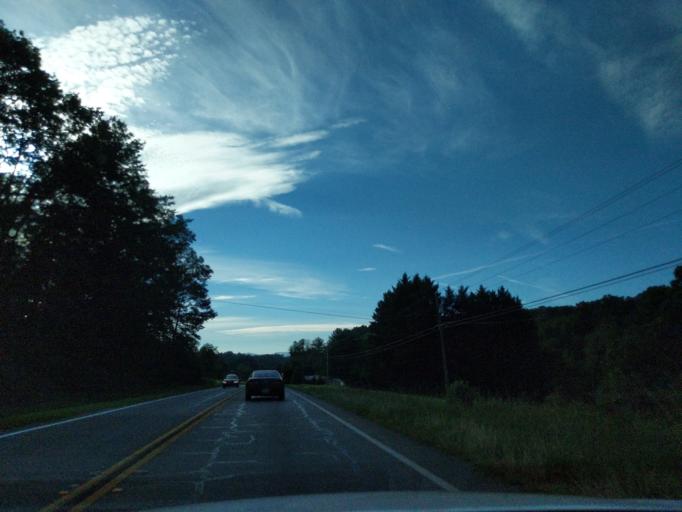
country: US
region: Georgia
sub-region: Fannin County
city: Blue Ridge
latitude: 34.8968
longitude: -84.3606
